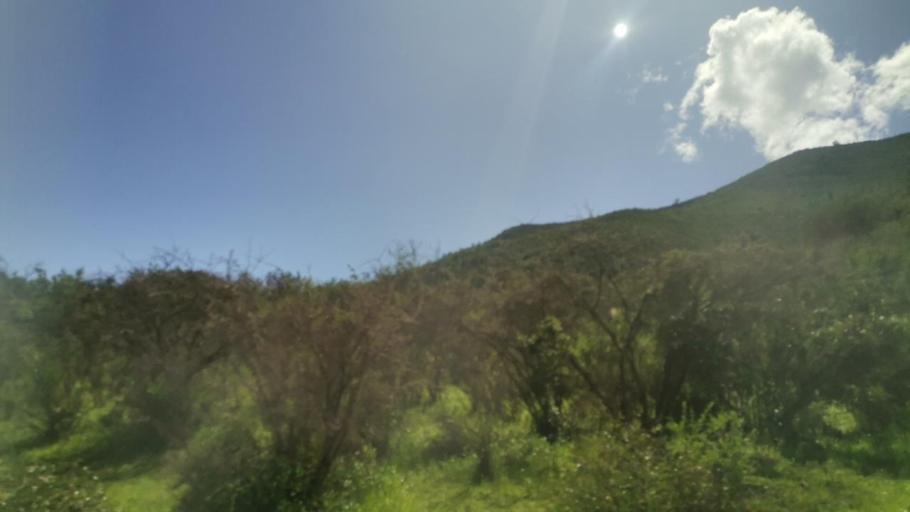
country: CL
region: Valparaiso
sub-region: Provincia de Marga Marga
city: Limache
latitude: -33.1974
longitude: -71.2704
